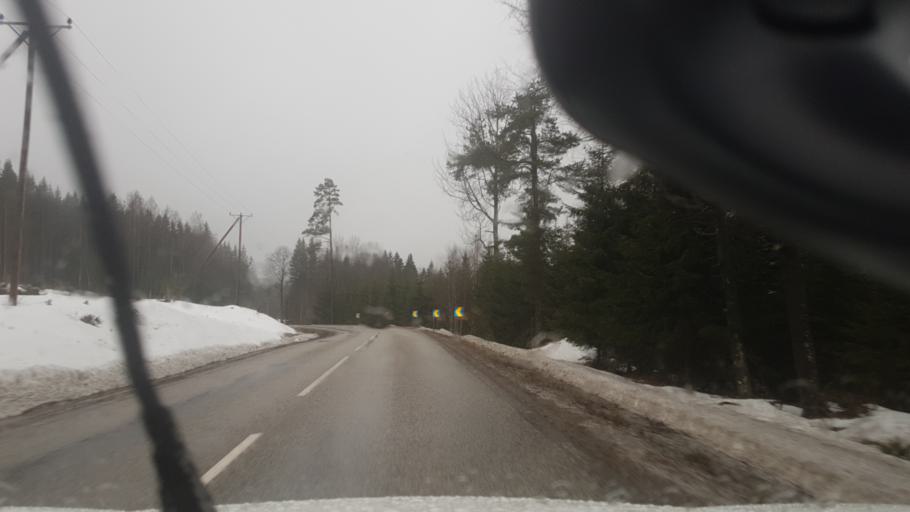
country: SE
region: Vaermland
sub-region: Arjangs Kommun
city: Arjaeng
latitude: 59.5714
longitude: 12.2077
